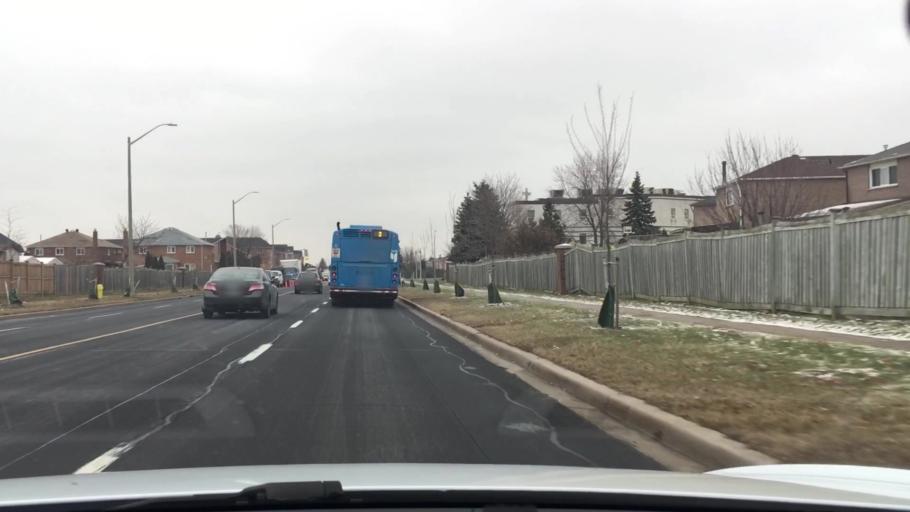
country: CA
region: Ontario
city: Markham
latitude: 43.8419
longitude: -79.2705
